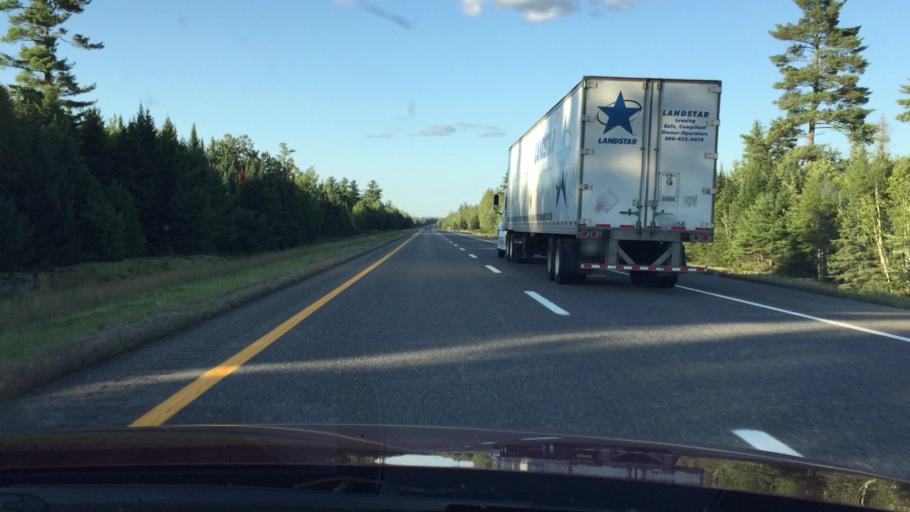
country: US
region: Maine
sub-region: Penobscot County
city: Patten
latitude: 46.0679
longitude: -68.2257
